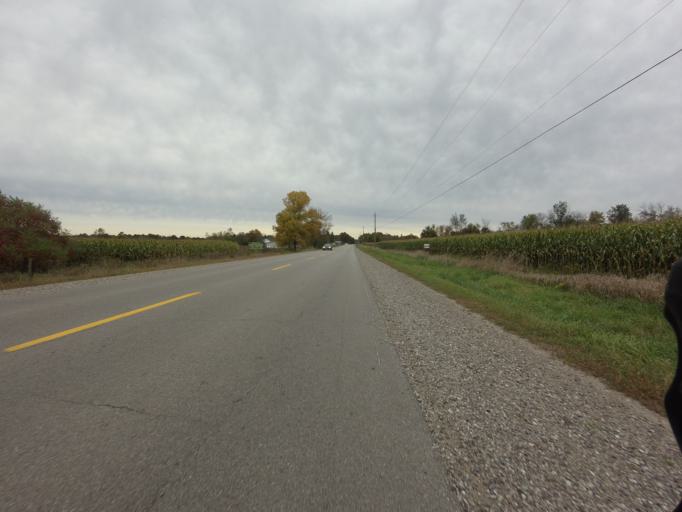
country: CA
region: Ontario
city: Gananoque
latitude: 44.5321
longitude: -76.1485
